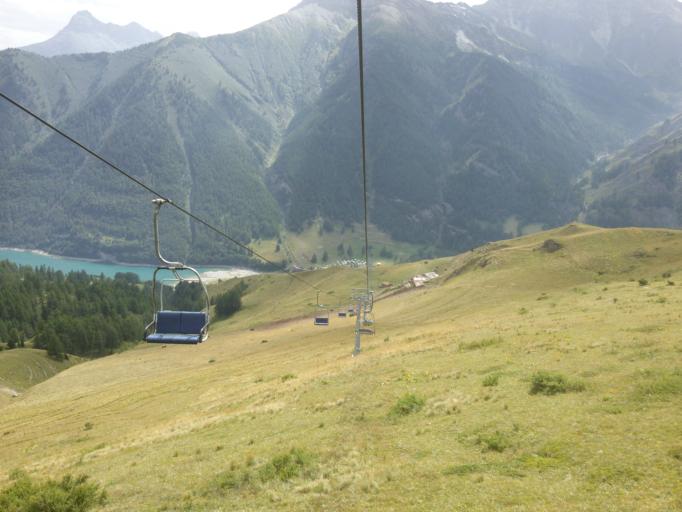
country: IT
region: Piedmont
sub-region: Provincia di Cuneo
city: Pontechianale
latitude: 44.6332
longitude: 7.0386
